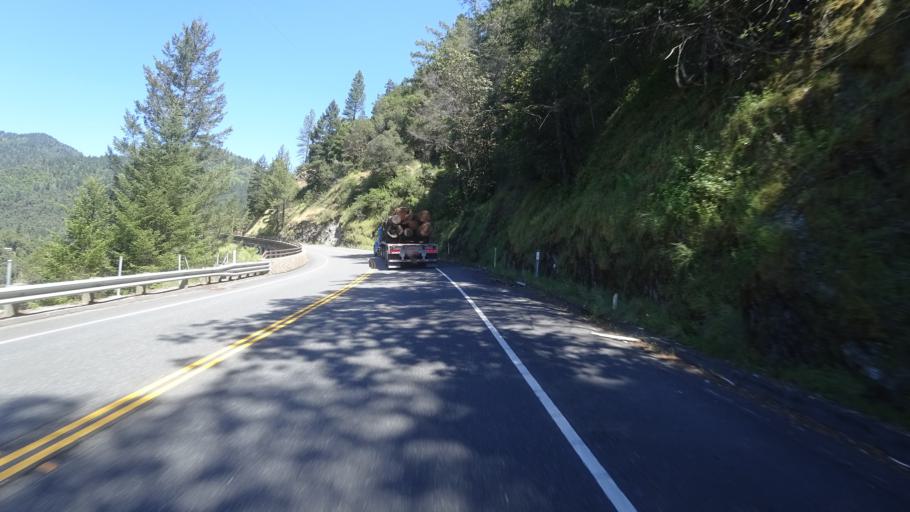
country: US
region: California
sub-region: Humboldt County
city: Willow Creek
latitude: 40.8910
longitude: -123.5648
